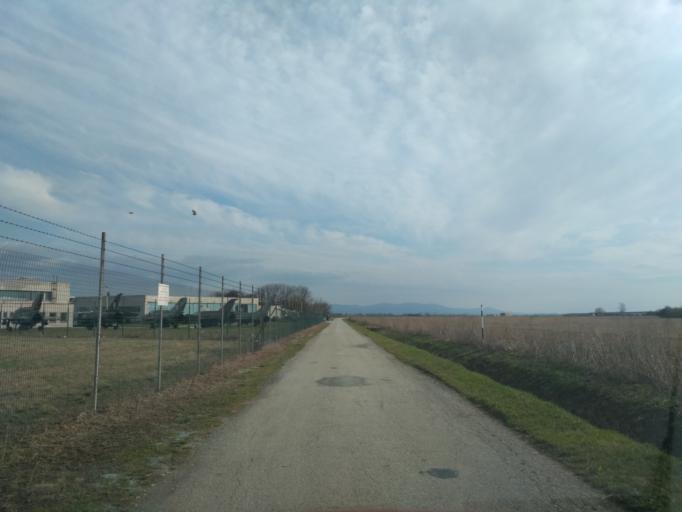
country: SK
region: Kosicky
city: Kosice
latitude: 48.6694
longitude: 21.2342
